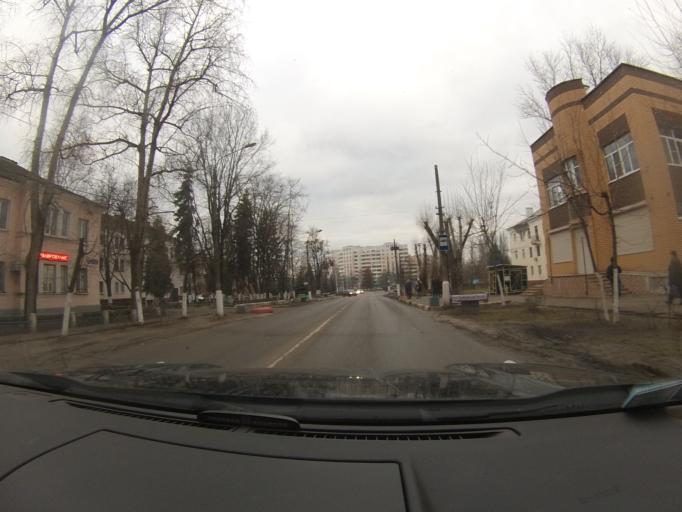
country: RU
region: Moskovskaya
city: Lopatinskiy
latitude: 55.3408
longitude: 38.7217
